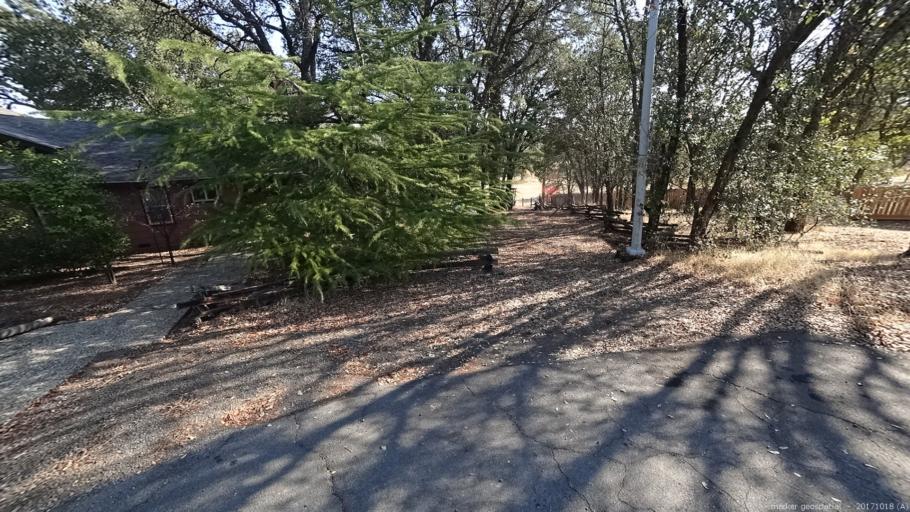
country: US
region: California
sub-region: Shasta County
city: Palo Cedro
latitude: 40.5489
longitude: -122.2987
